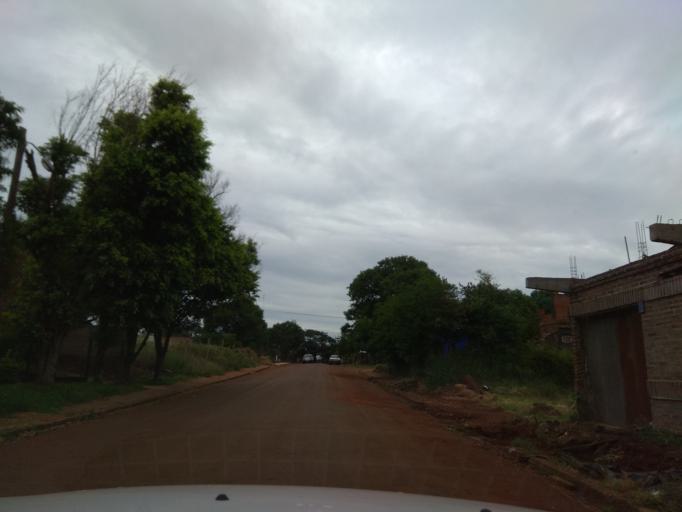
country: AR
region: Misiones
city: Garupa
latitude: -27.4443
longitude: -55.8685
